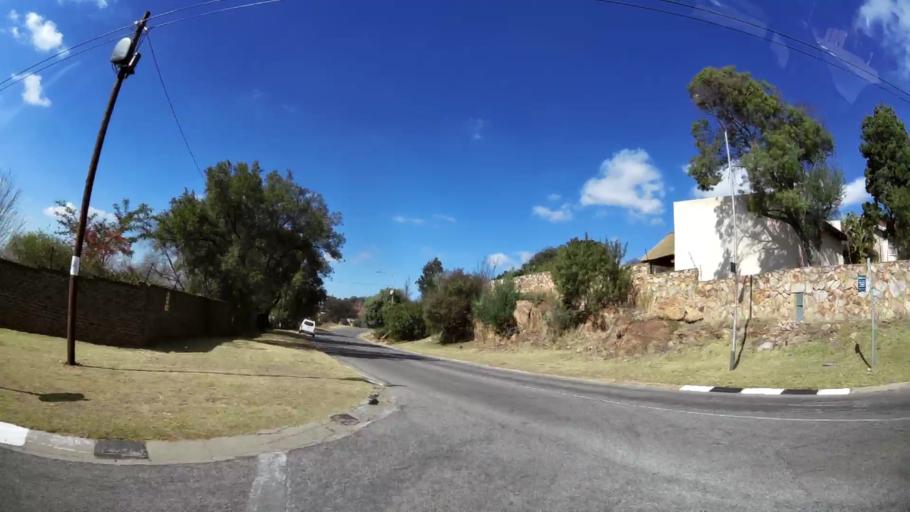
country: ZA
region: Gauteng
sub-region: City of Johannesburg Metropolitan Municipality
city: Roodepoort
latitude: -26.1172
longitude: 27.8409
